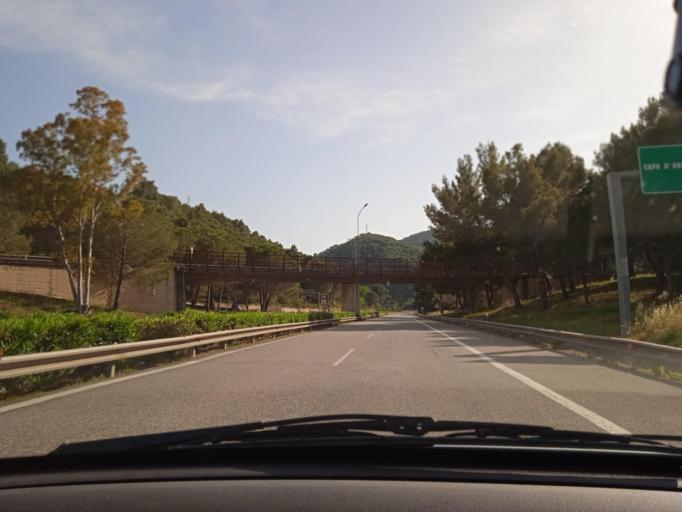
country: IT
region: Sicily
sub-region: Messina
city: Brolo
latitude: 38.1482
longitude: 14.8280
